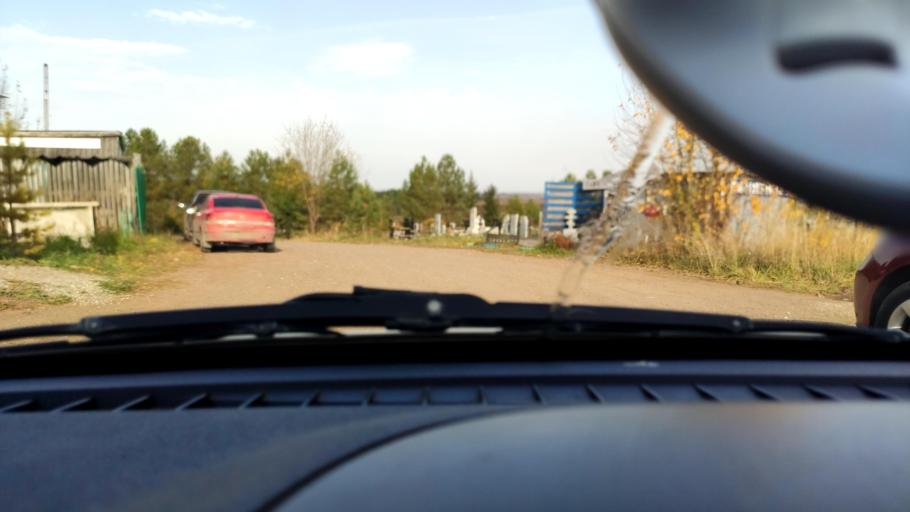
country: RU
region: Perm
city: Kultayevo
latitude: 57.8586
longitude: 55.8688
